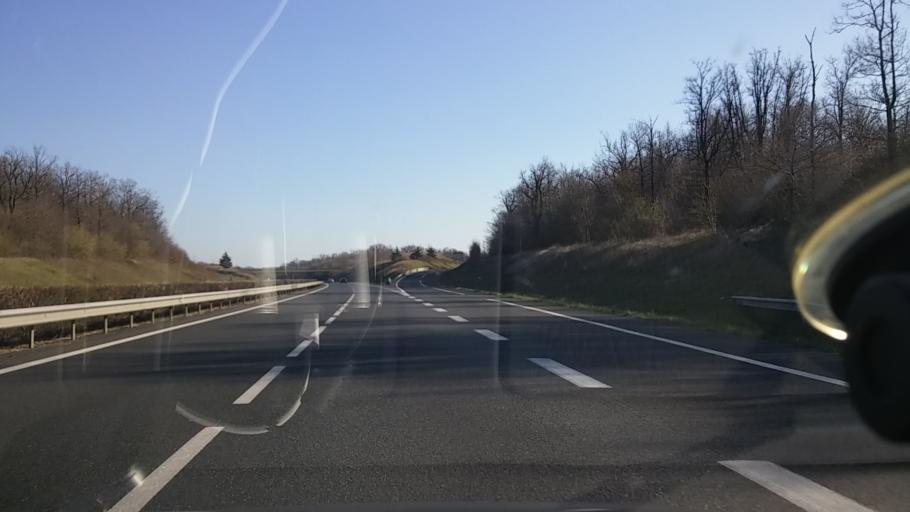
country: FR
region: Centre
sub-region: Departement de l'Indre
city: Saint-Maur
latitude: 46.7989
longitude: 1.6167
